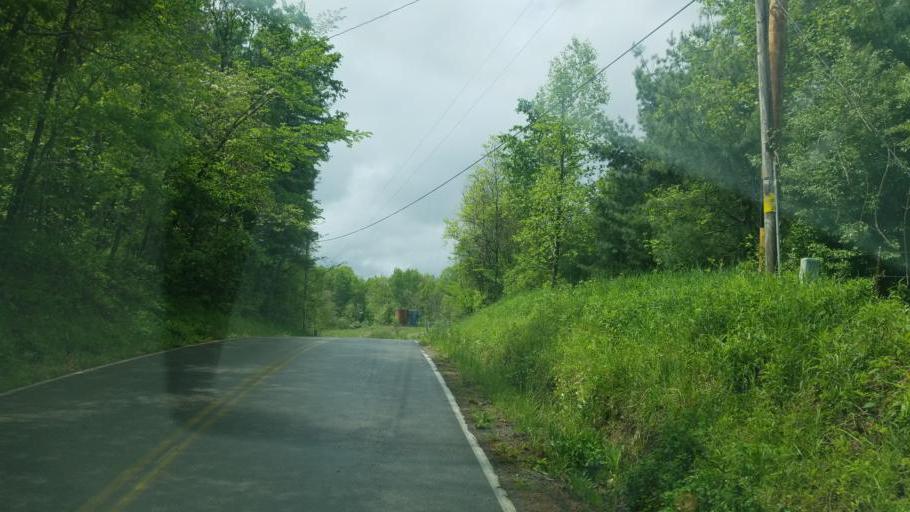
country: US
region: Ohio
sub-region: Tuscarawas County
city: Rockford
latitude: 40.4258
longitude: -81.2331
